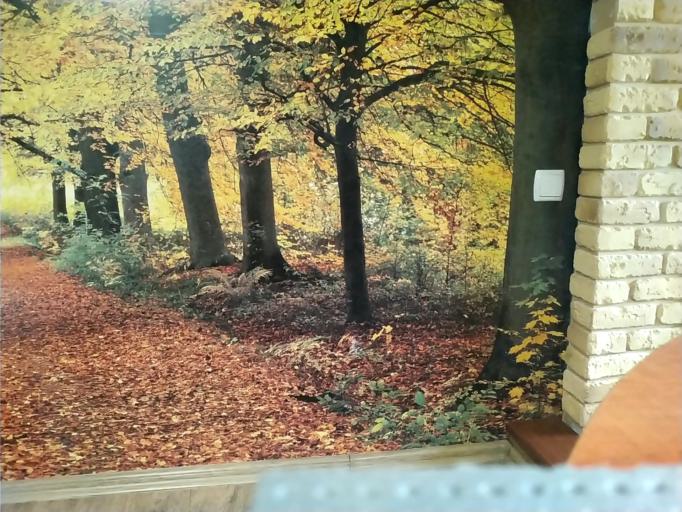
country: RU
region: Tverskaya
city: Staritsa
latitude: 56.5235
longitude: 35.0678
